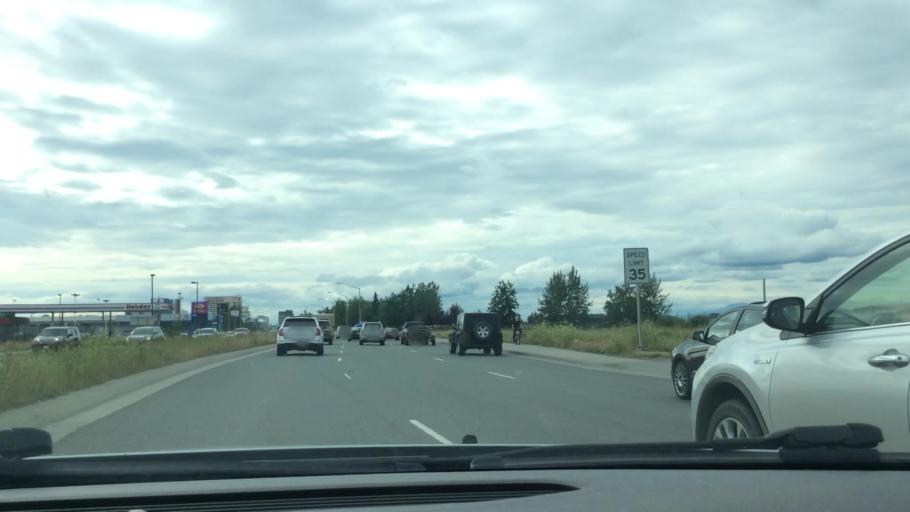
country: US
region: Alaska
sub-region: Anchorage Municipality
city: Anchorage
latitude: 61.2156
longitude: -149.8549
